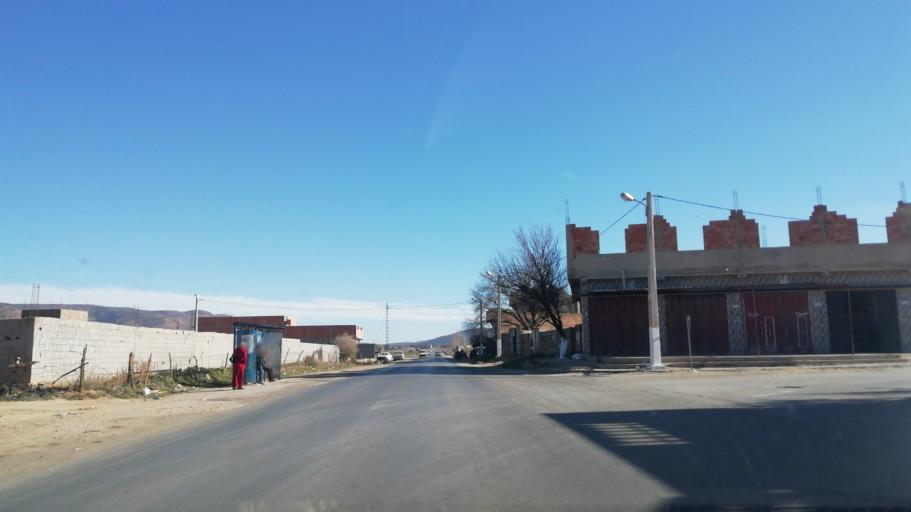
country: DZ
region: Tlemcen
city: Sebdou
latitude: 34.6646
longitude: -1.2890
